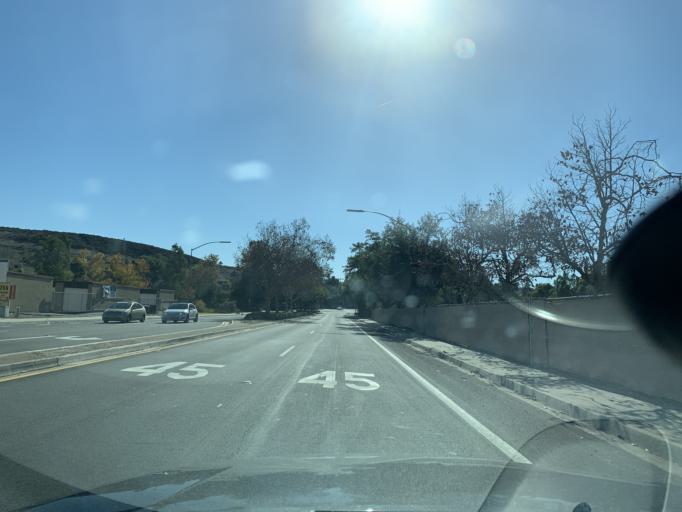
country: US
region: California
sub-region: San Diego County
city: Poway
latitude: 32.9499
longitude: -117.0627
